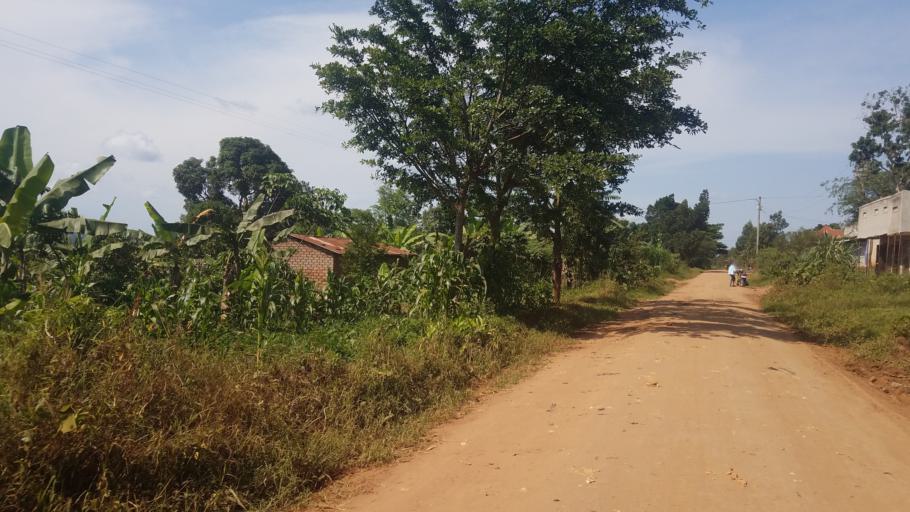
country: UG
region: Central Region
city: Masaka
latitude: -0.3307
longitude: 31.7096
